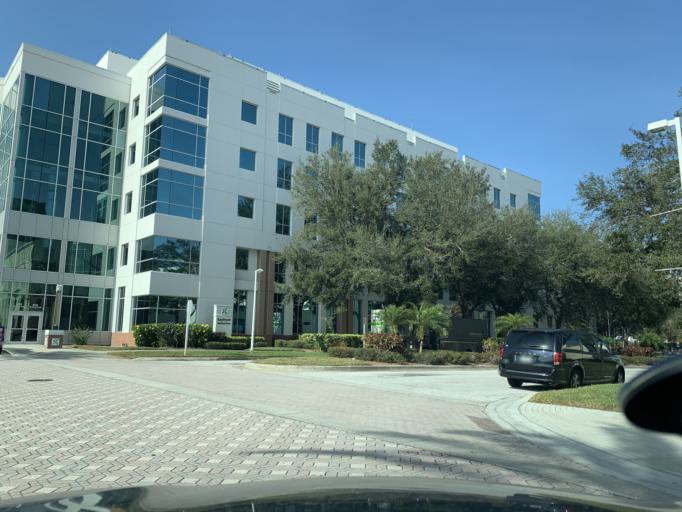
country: US
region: Florida
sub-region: Pinellas County
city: Saint Petersburg
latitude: 27.7634
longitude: -82.6430
